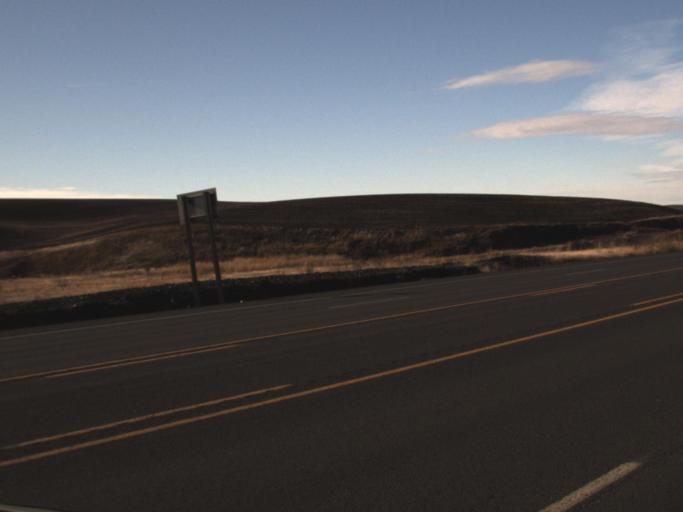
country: US
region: Idaho
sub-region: Latah County
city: Moscow
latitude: 46.7386
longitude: -117.0635
